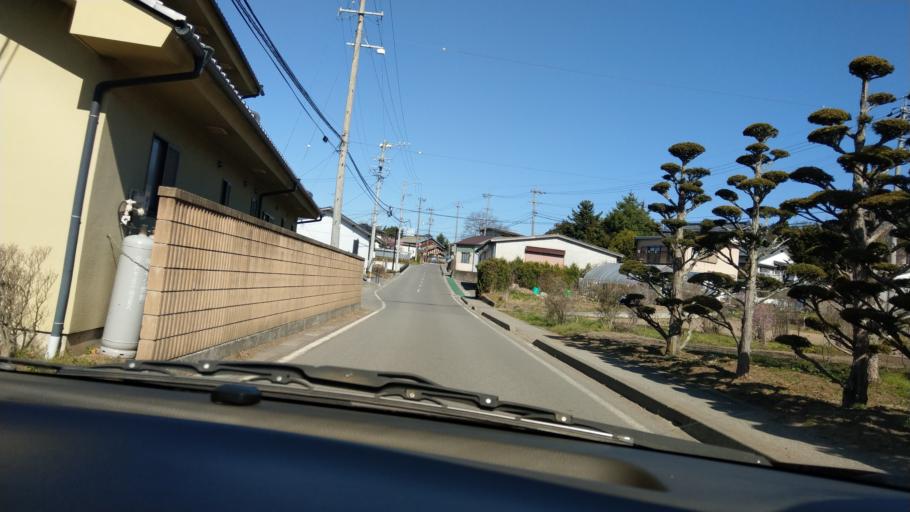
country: JP
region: Nagano
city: Komoro
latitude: 36.3345
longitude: 138.4968
